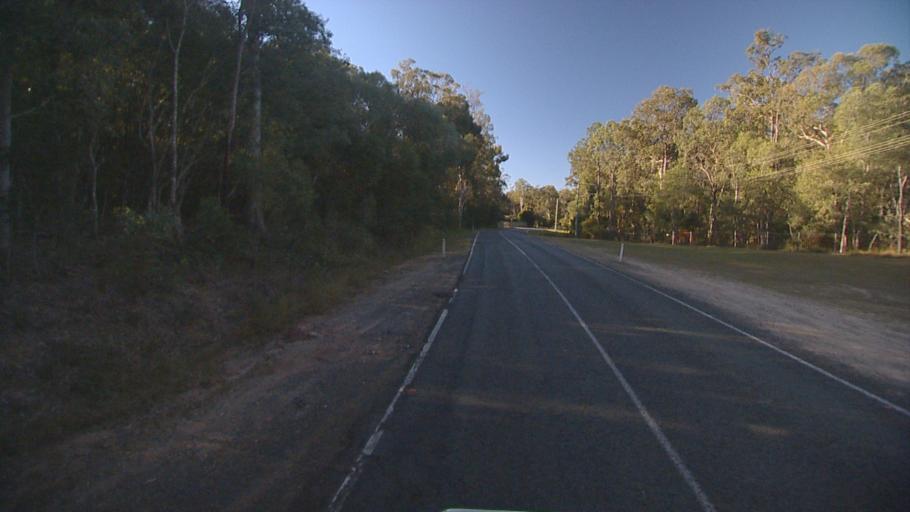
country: AU
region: Queensland
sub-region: Logan
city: Chambers Flat
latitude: -27.7560
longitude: 153.0494
